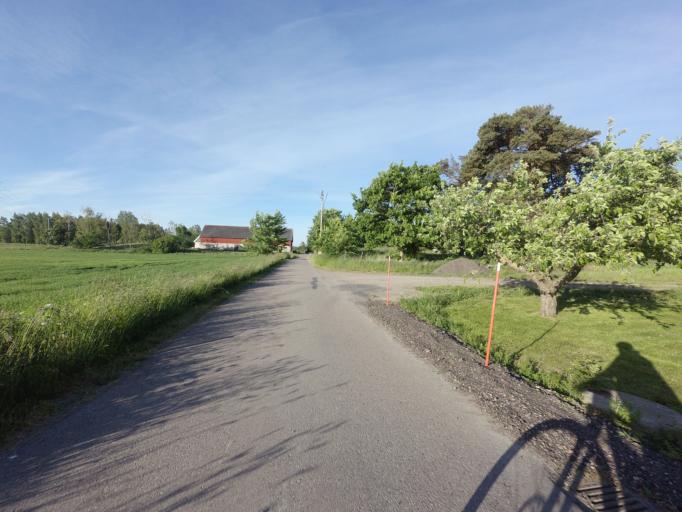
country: SE
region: Skane
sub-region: Hoganas Kommun
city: Hoganas
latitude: 56.2440
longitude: 12.6505
